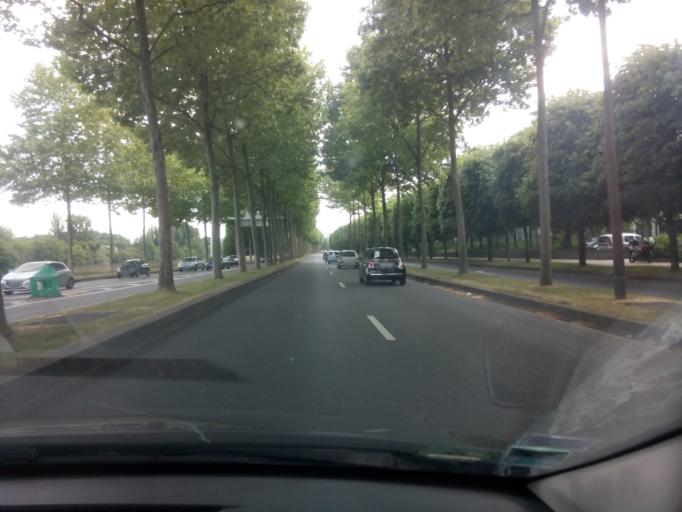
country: FR
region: Ile-de-France
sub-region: Departement des Hauts-de-Seine
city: Puteaux
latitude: 48.8770
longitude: 2.2407
